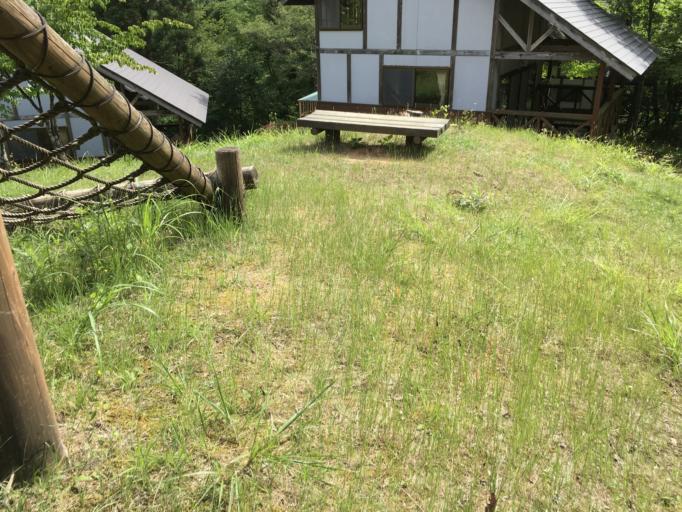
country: JP
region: Miyagi
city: Wakuya
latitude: 38.6863
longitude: 141.3459
